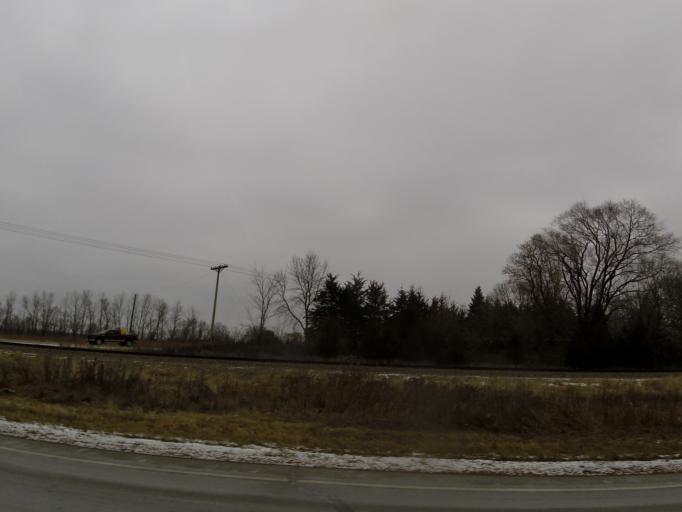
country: US
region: Minnesota
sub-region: Hennepin County
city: Independence
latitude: 45.0274
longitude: -93.7185
